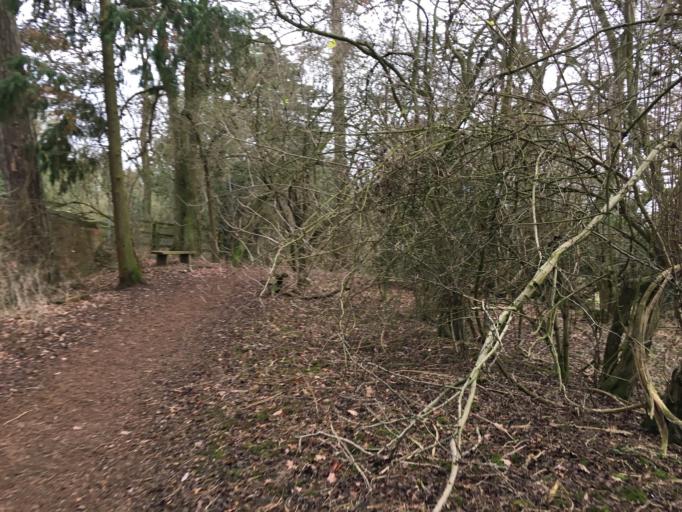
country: GB
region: England
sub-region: Warwickshire
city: Rugby
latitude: 52.3936
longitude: -1.2573
